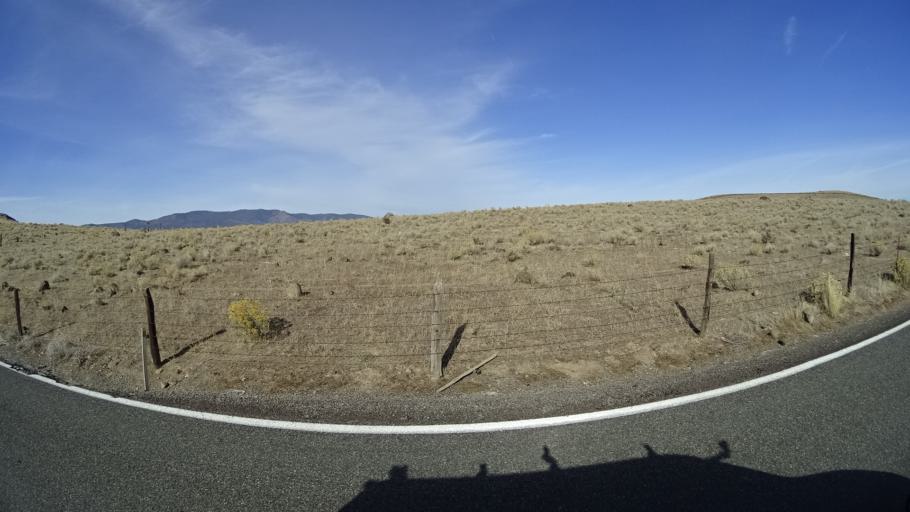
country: US
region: California
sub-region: Siskiyou County
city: Weed
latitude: 41.5472
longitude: -122.4985
